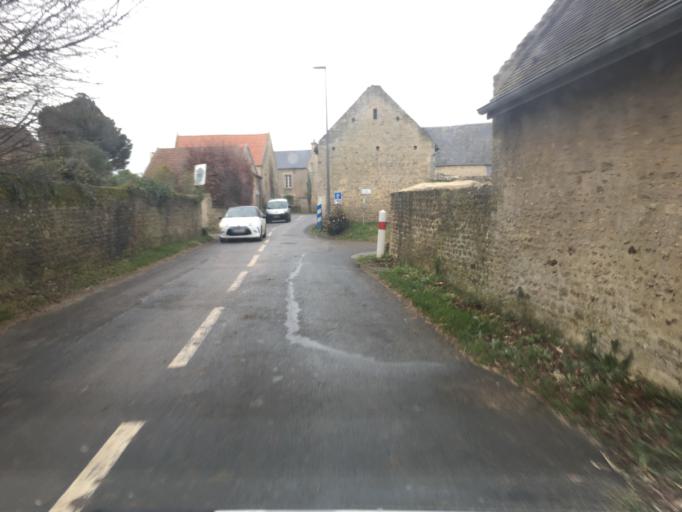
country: FR
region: Lower Normandy
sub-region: Departement du Calvados
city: Saint-Vigor-le-Grand
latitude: 49.3368
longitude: -0.6547
